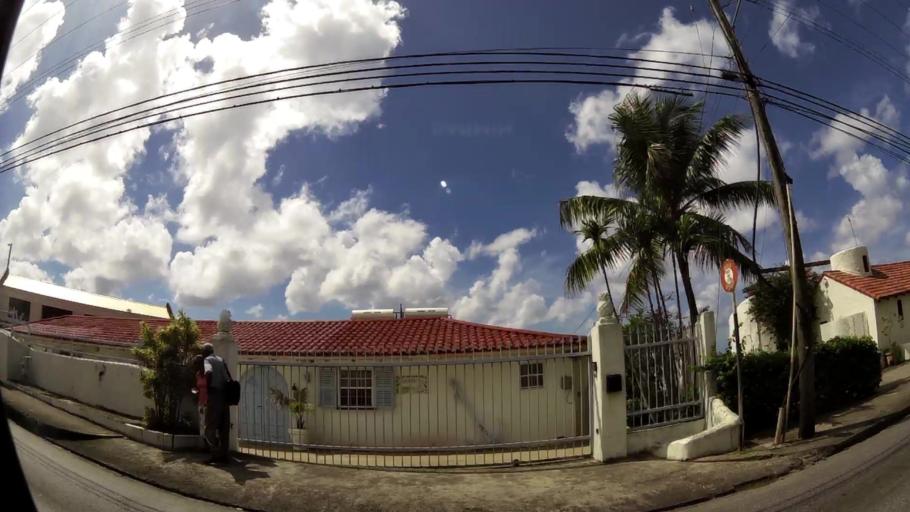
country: BB
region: Saint Michael
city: Bridgetown
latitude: 13.1373
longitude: -59.6360
